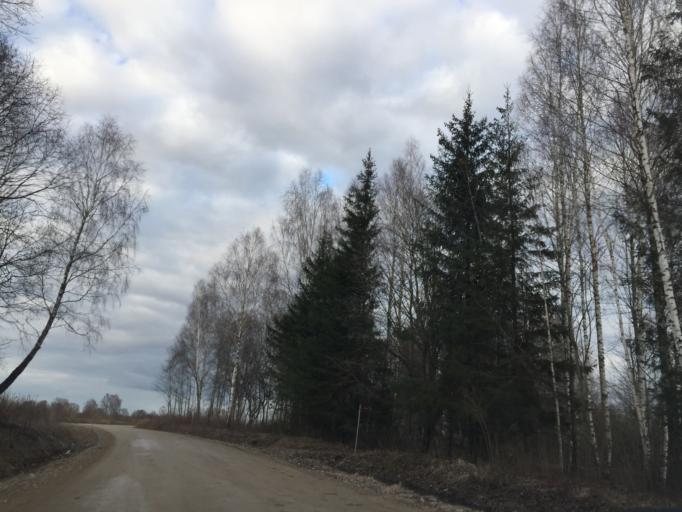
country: LV
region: Jaunjelgava
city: Jaunjelgava
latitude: 56.6057
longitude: 25.0650
